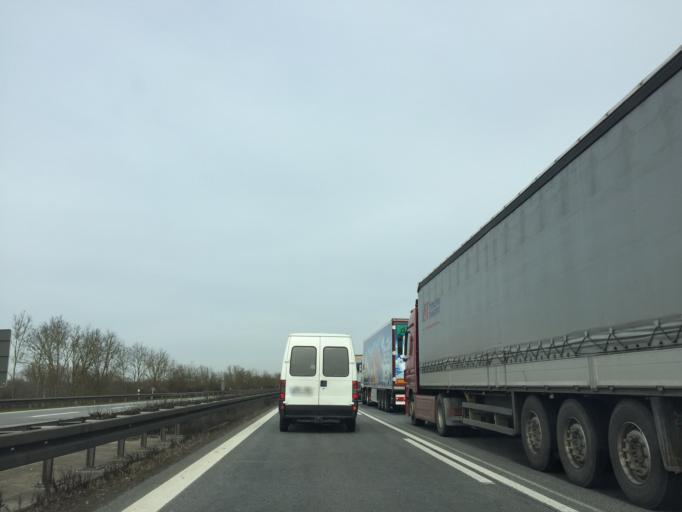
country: AT
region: Upper Austria
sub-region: Politischer Bezirk Scharding
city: Scharding
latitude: 48.4384
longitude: 13.3760
